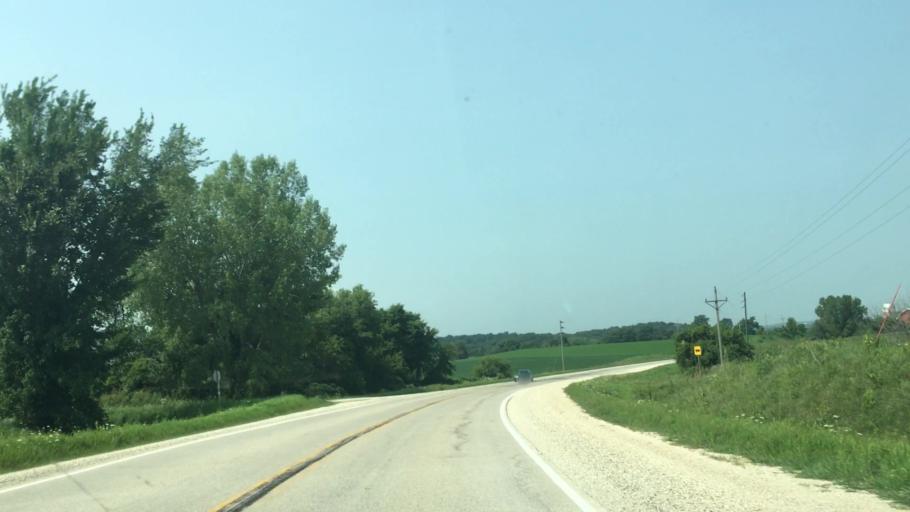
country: US
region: Iowa
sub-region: Fayette County
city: West Union
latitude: 43.0995
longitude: -91.8683
